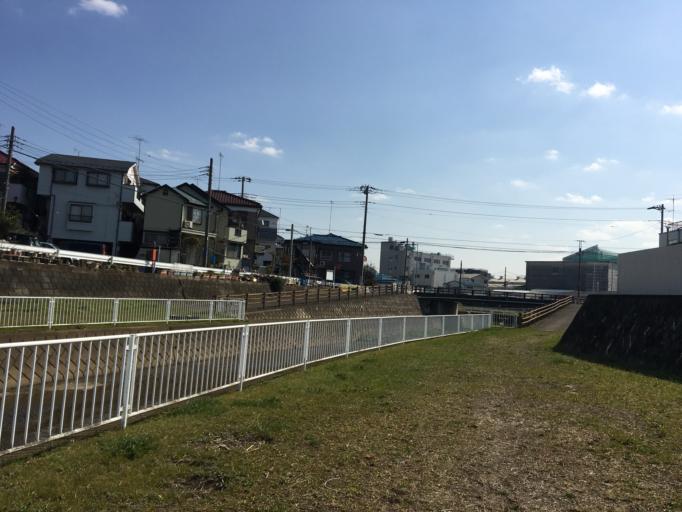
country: JP
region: Saitama
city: Shiki
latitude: 35.8412
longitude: 139.5754
